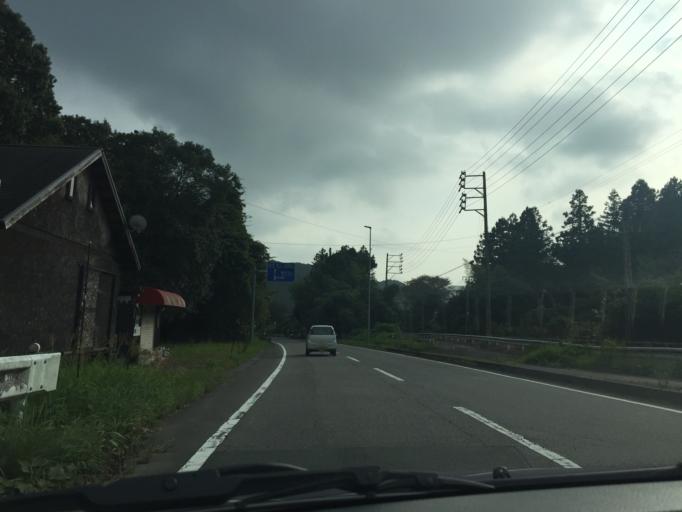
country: JP
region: Aichi
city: Shinshiro
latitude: 34.9481
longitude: 137.6012
